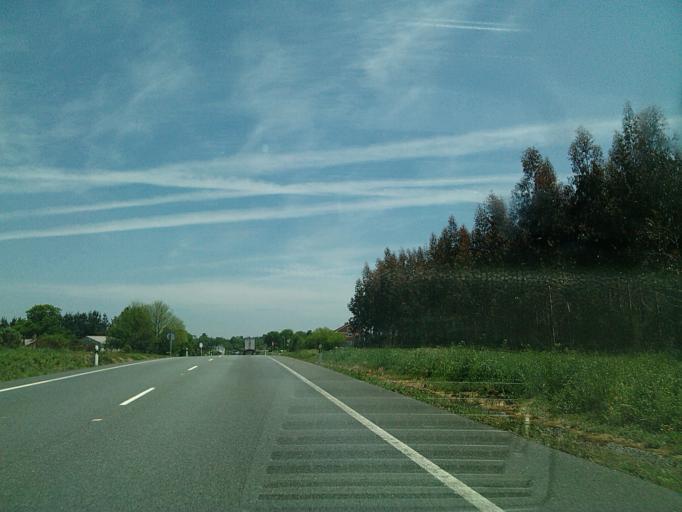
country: ES
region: Galicia
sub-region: Provincia da Coruna
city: Vilasantar
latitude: 43.1001
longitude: -8.1686
